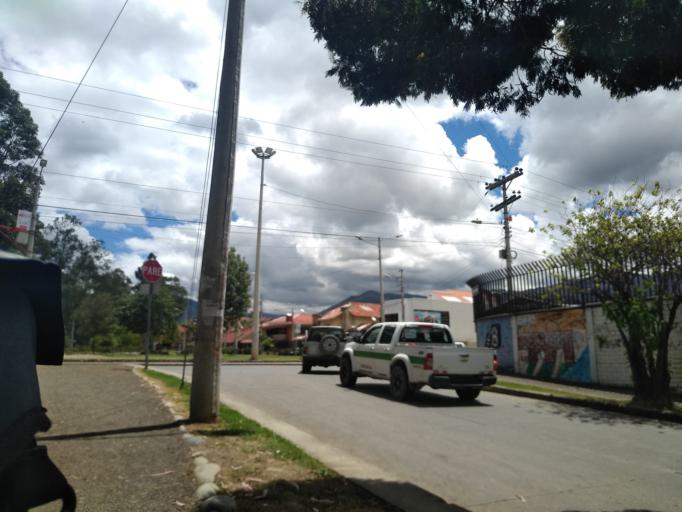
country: EC
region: Azuay
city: Cuenca
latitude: -2.8900
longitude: -79.0356
